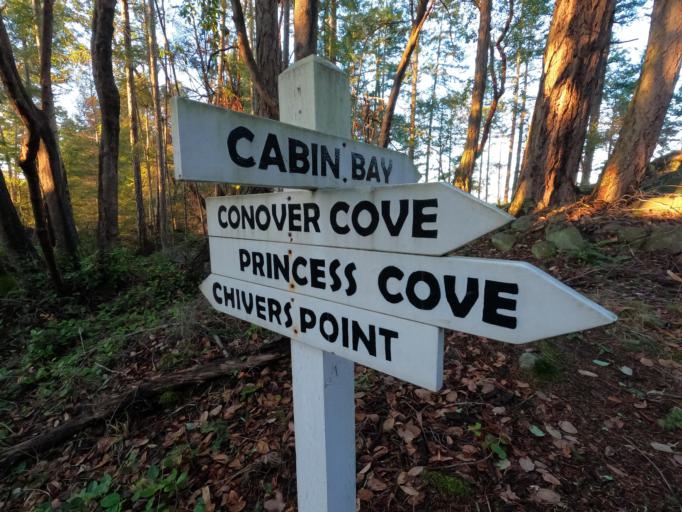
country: CA
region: British Columbia
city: North Cowichan
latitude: 48.9512
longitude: -123.5660
